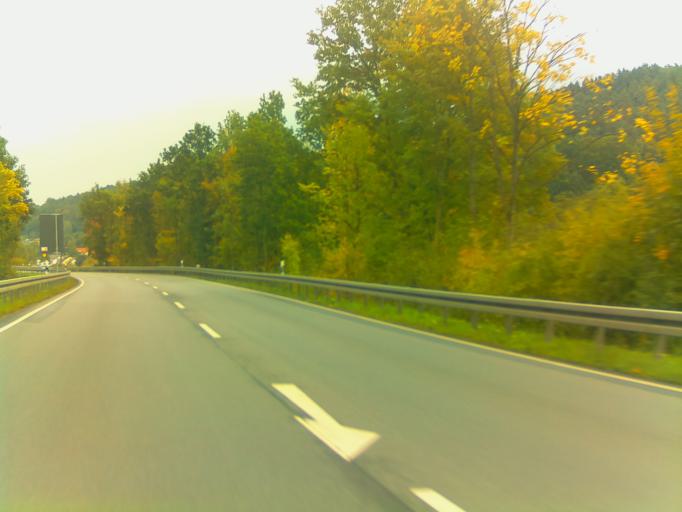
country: DE
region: Hesse
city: Hochst im Odenwald
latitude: 49.8152
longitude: 9.0270
